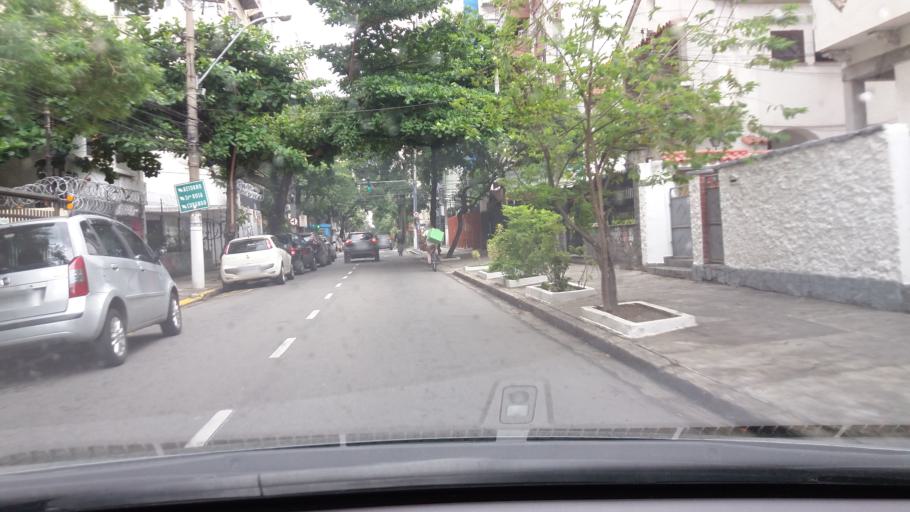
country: BR
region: Rio de Janeiro
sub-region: Niteroi
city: Niteroi
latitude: -22.9014
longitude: -43.1098
